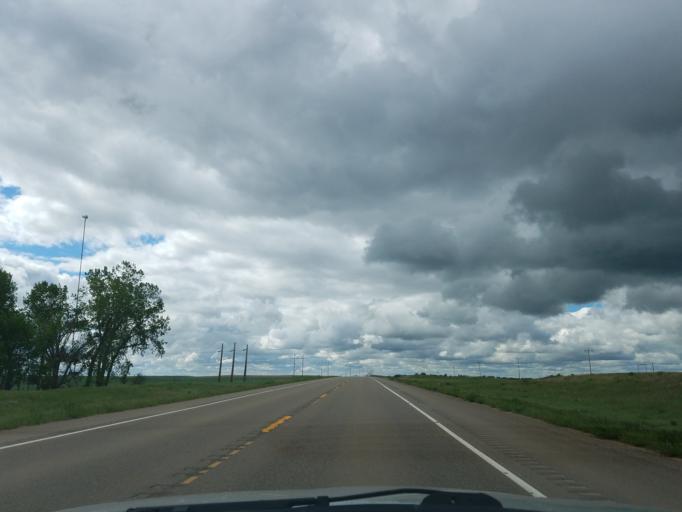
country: US
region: North Dakota
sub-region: McKenzie County
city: Watford City
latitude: 47.4520
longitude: -103.2475
